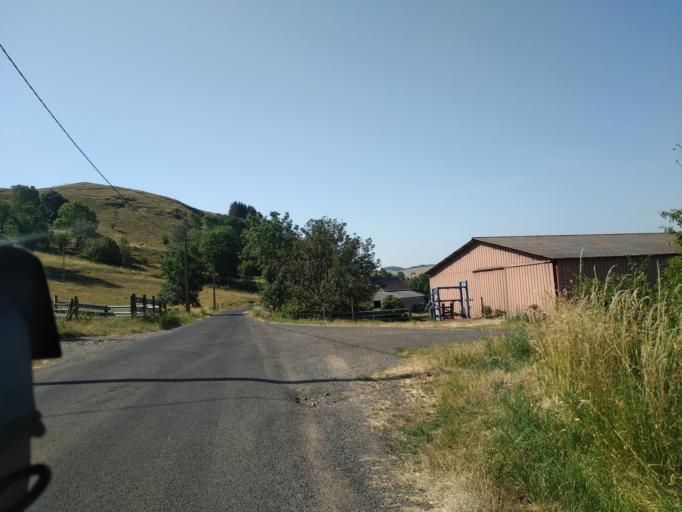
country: FR
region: Auvergne
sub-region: Departement du Cantal
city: Riom-es-Montagnes
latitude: 45.2472
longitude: 2.7427
